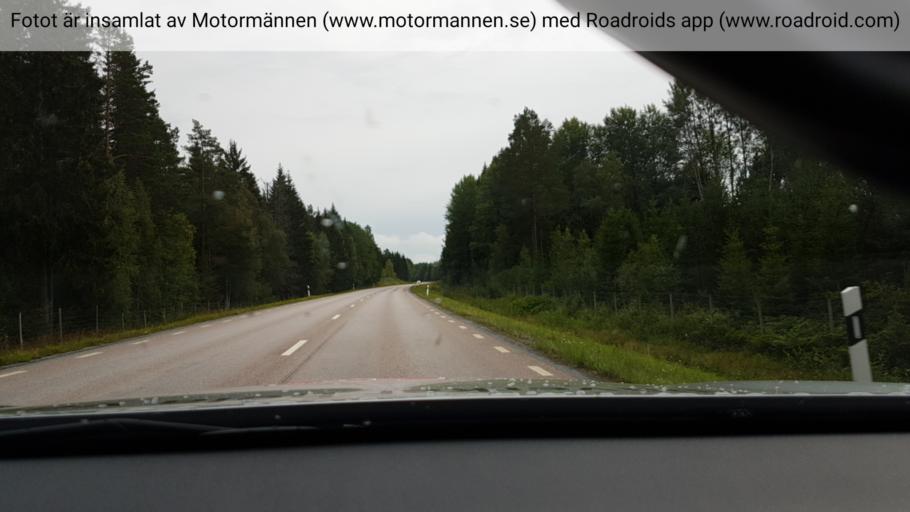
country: SE
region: Uppsala
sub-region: Osthammars Kommun
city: Osterbybruk
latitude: 60.4135
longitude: 17.8655
